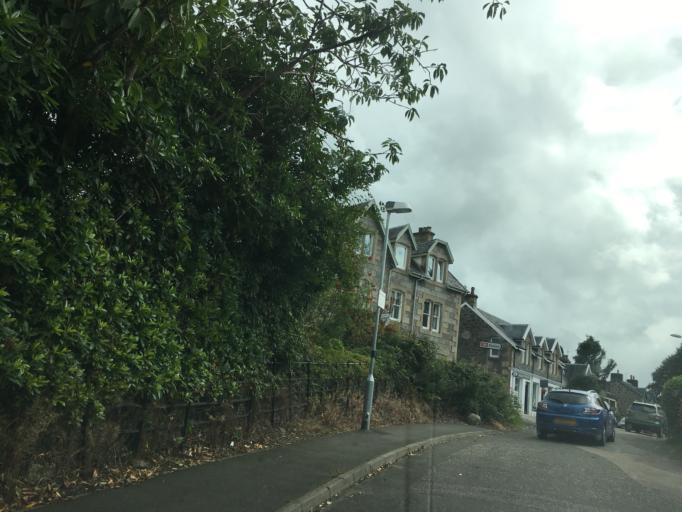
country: GB
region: Scotland
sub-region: Argyll and Bute
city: Oban
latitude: 56.4305
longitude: -5.2387
